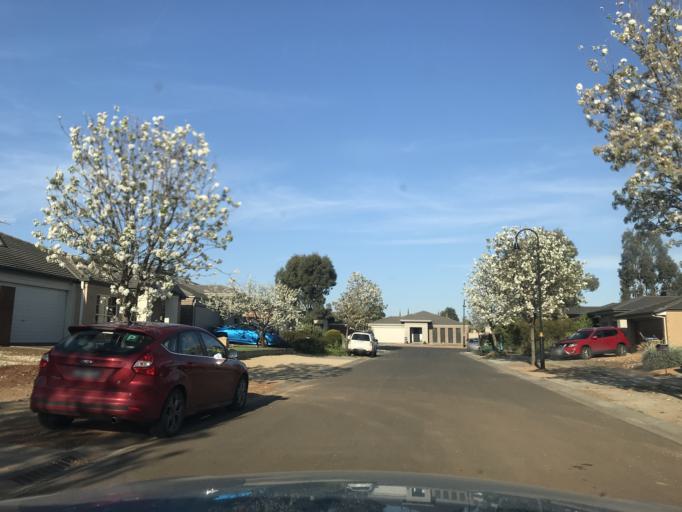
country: AU
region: Victoria
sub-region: Wyndham
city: Williams Landing
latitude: -37.8597
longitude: 144.7211
